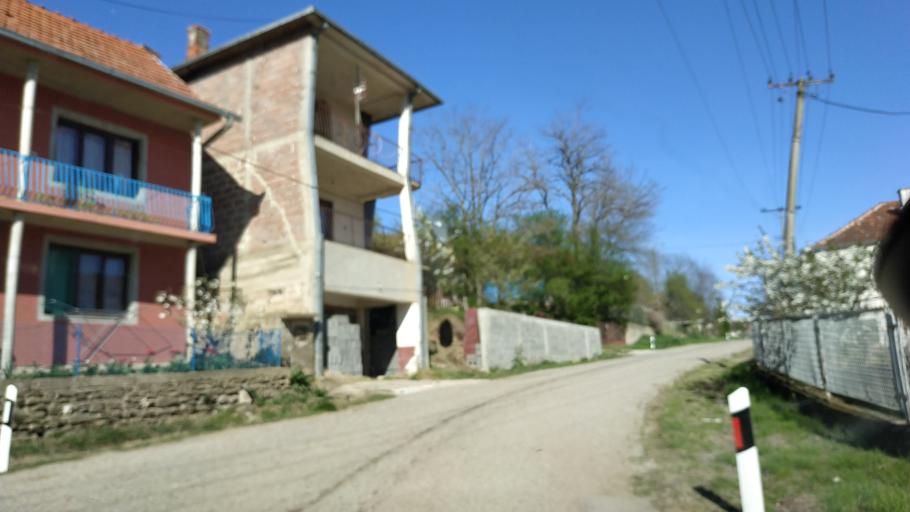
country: RS
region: Central Serbia
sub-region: Nisavski Okrug
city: Aleksinac
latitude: 43.4756
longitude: 21.6448
